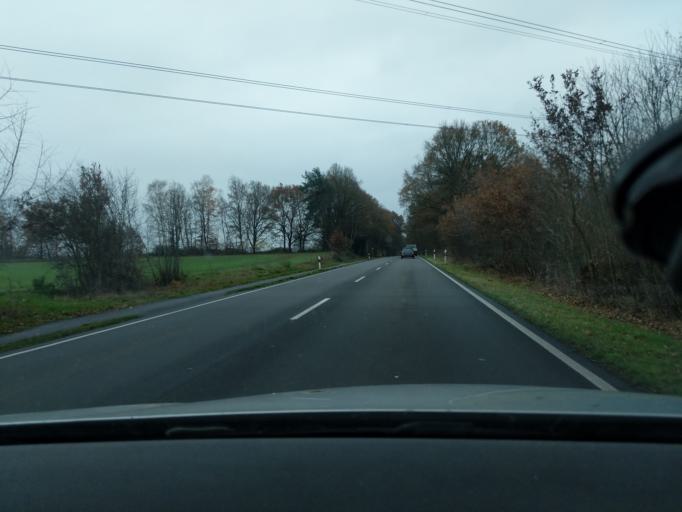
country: DE
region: Lower Saxony
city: Gyhum
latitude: 53.2222
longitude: 9.2932
